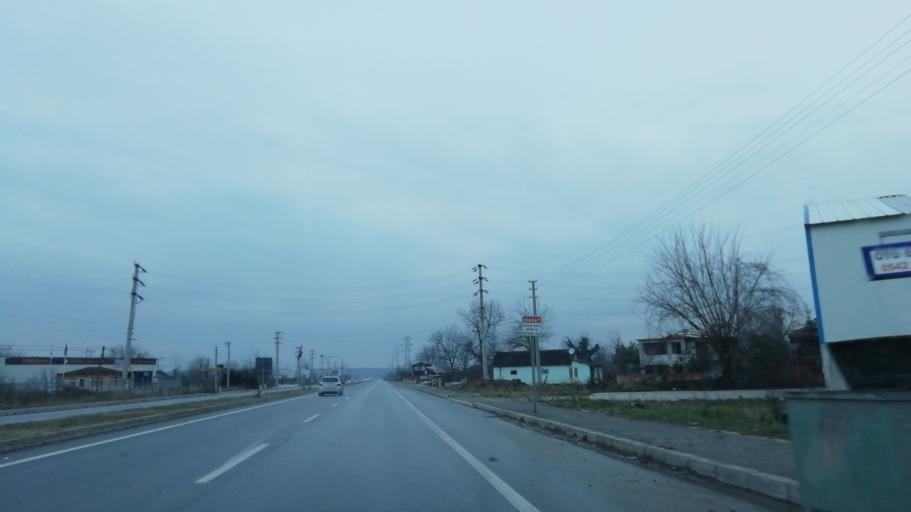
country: TR
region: Sakarya
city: Akyazi
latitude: 40.6356
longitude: 30.6255
